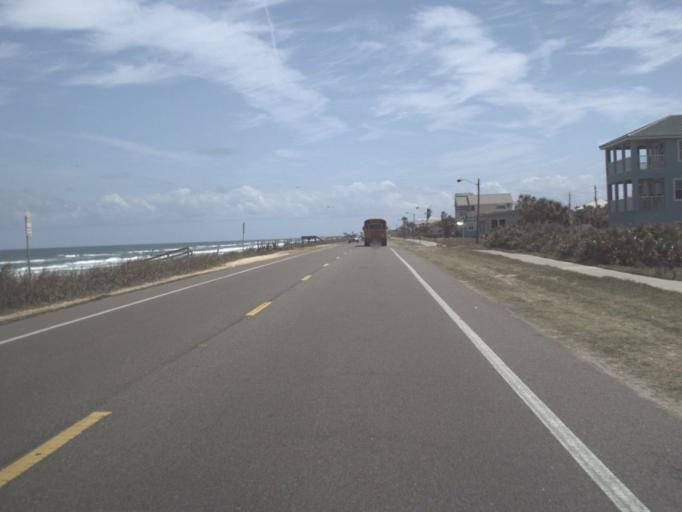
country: US
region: Florida
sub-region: Flagler County
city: Flagler Beach
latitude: 29.5049
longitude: -81.1391
